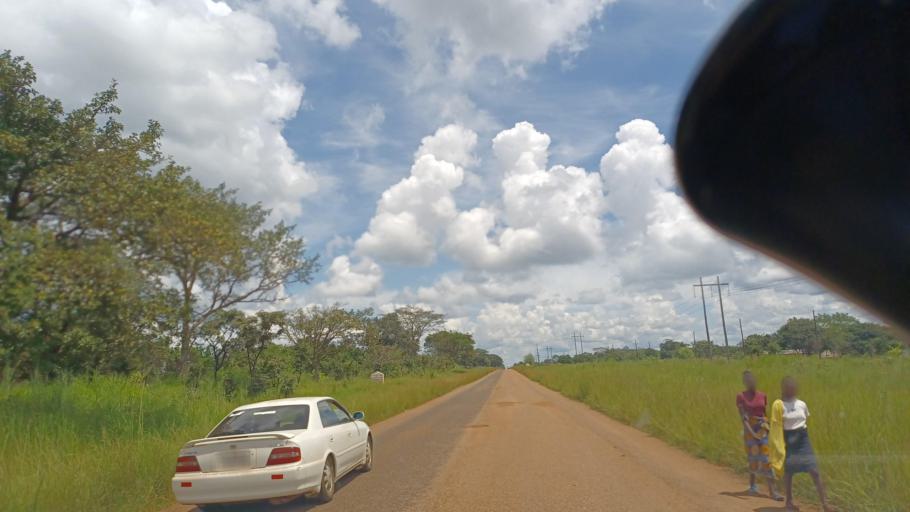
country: ZM
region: North-Western
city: Solwezi
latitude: -12.4857
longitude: 26.1944
